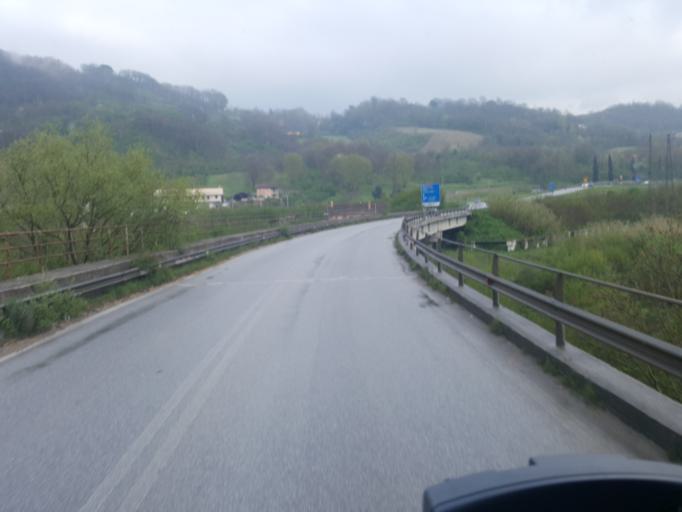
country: IT
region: Campania
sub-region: Provincia di Avellino
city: Manocalzati
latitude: 40.9384
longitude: 14.8282
